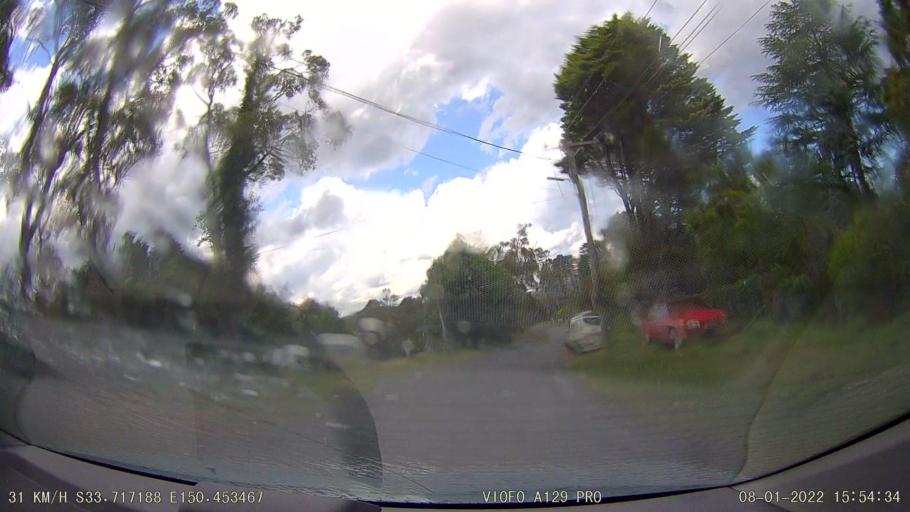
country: AU
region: New South Wales
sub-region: Blue Mountains Municipality
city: Hazelbrook
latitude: -33.7172
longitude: 150.4534
